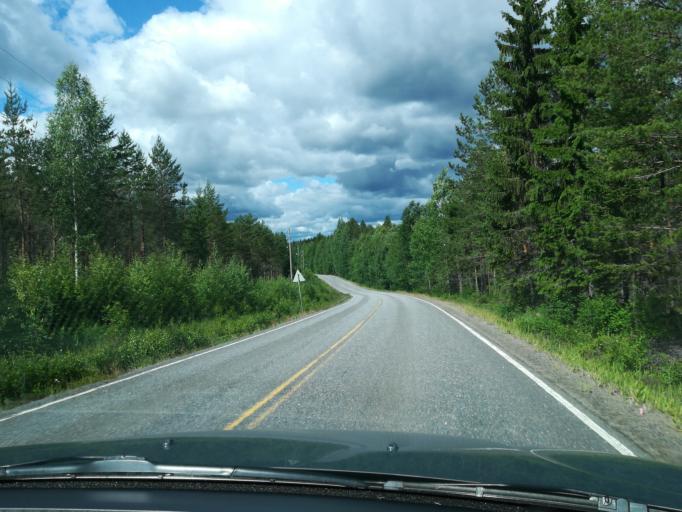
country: FI
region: Southern Savonia
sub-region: Mikkeli
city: Maentyharju
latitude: 61.3627
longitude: 27.0571
